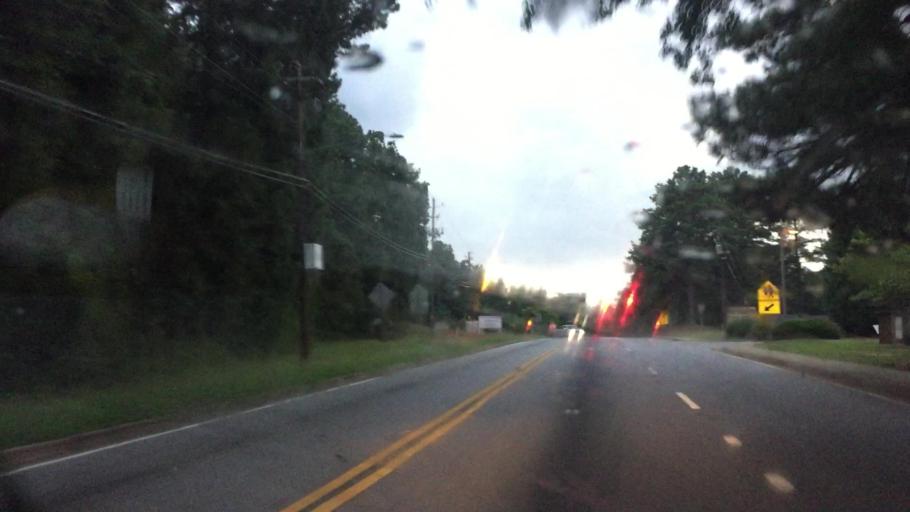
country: US
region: Georgia
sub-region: Clayton County
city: Riverdale
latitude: 33.5568
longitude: -84.4010
